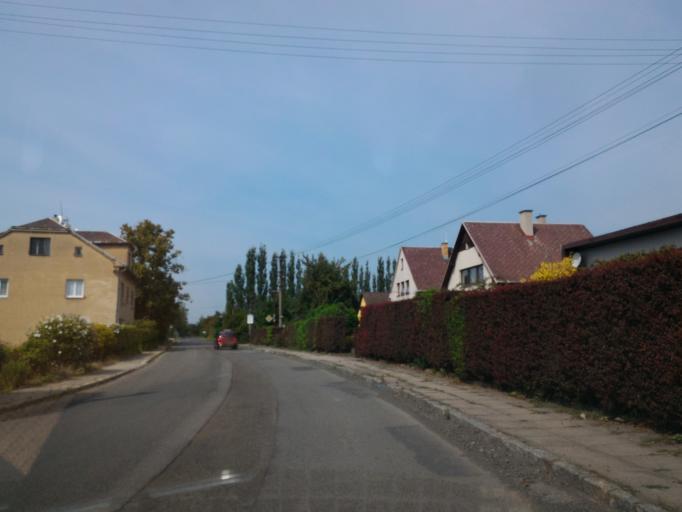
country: CZ
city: Ohrazenice
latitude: 50.5829
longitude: 15.1088
